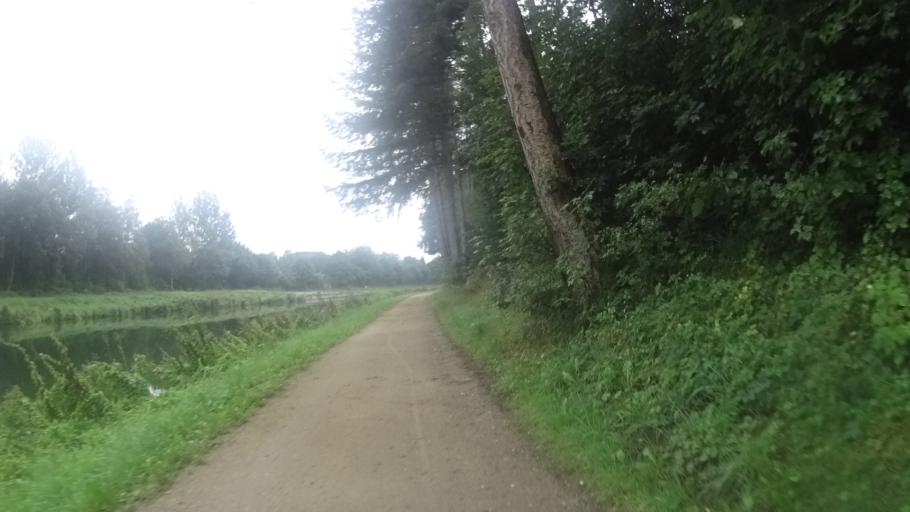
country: DE
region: Schleswig-Holstein
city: Grambek
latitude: 53.5810
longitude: 10.6721
